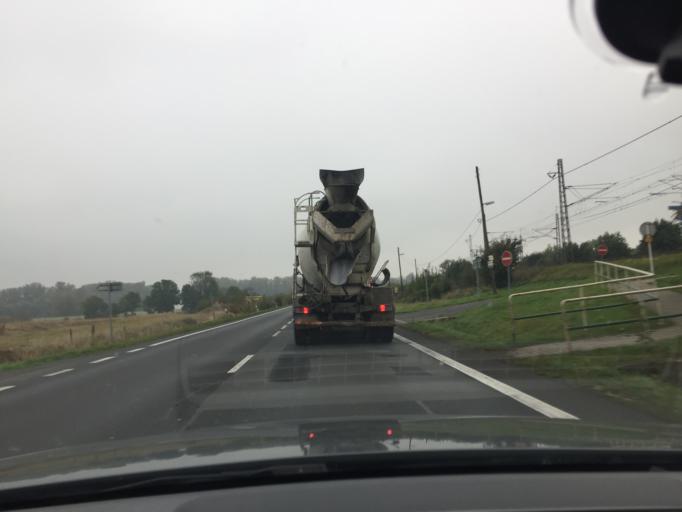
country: CZ
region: Ustecky
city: Lovosice
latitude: 50.5381
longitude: 14.0570
